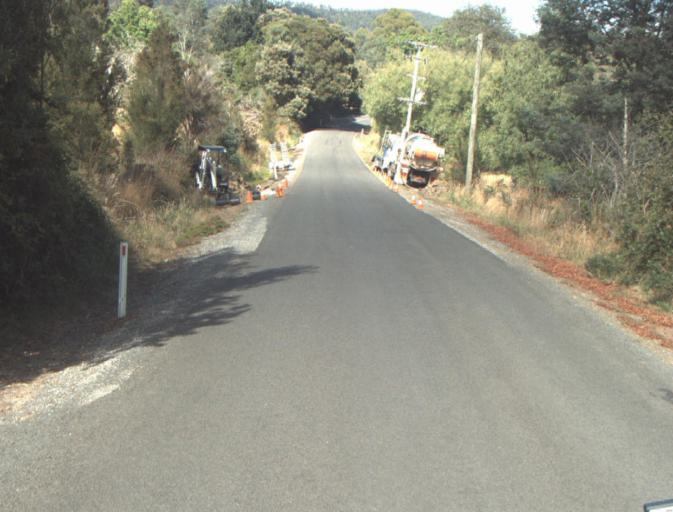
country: AU
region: Tasmania
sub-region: Launceston
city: Mayfield
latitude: -41.2583
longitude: 147.1812
